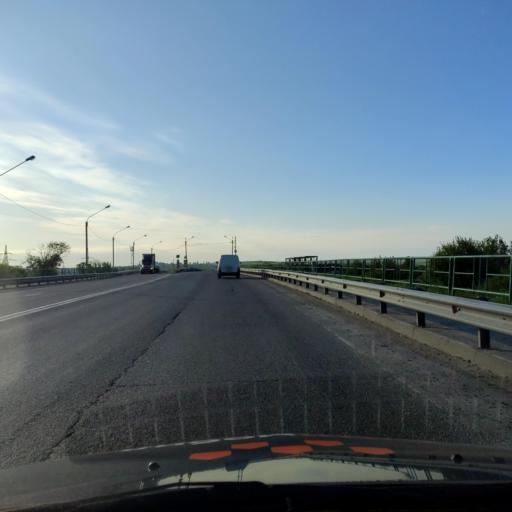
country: RU
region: Lipetsk
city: Yelets
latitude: 52.5922
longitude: 38.4905
